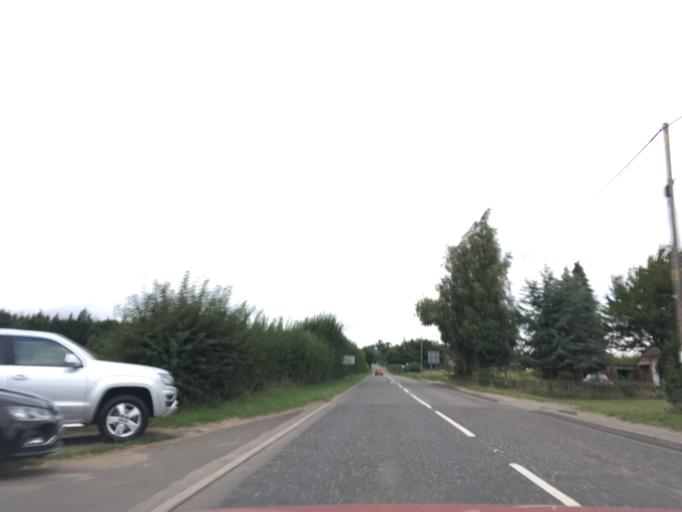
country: GB
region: England
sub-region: Wiltshire
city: Calne
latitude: 51.3972
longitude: -2.0453
